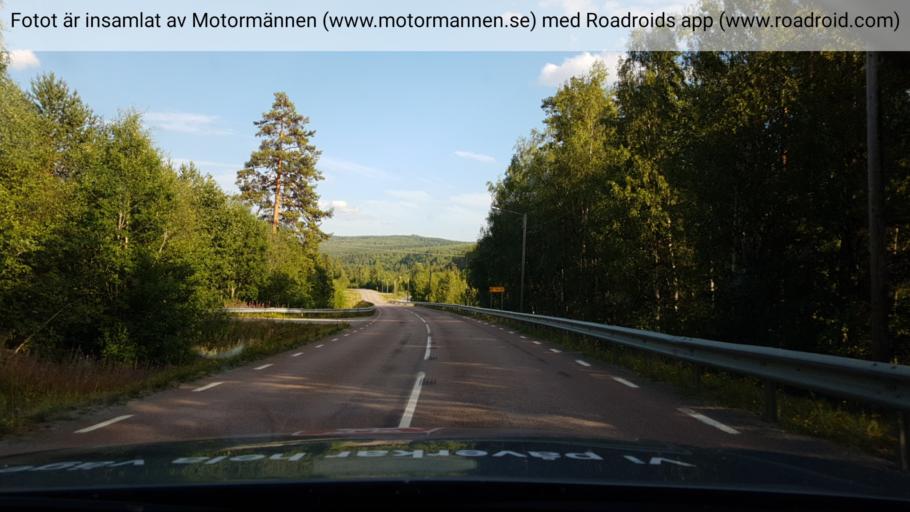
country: SE
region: Vaesternorrland
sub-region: Solleftea Kommun
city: As
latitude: 63.5835
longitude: 16.3383
